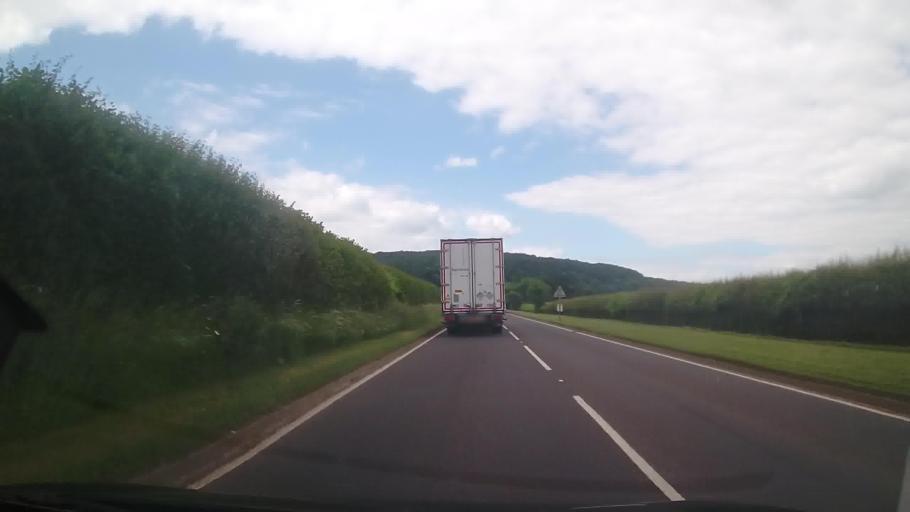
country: GB
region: England
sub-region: Herefordshire
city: Dinmore
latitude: 52.1437
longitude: -2.7280
